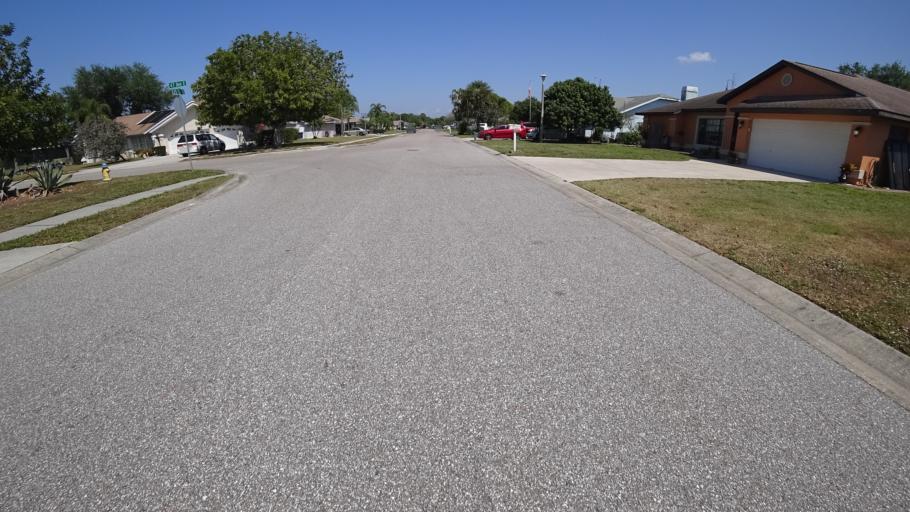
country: US
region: Florida
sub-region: Manatee County
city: Samoset
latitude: 27.4541
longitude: -82.5182
